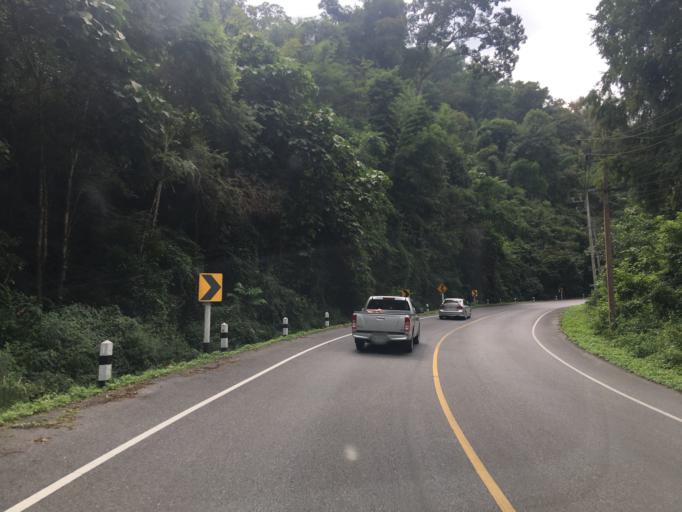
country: TH
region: Nan
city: Ban Luang
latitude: 18.8743
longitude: 100.4996
